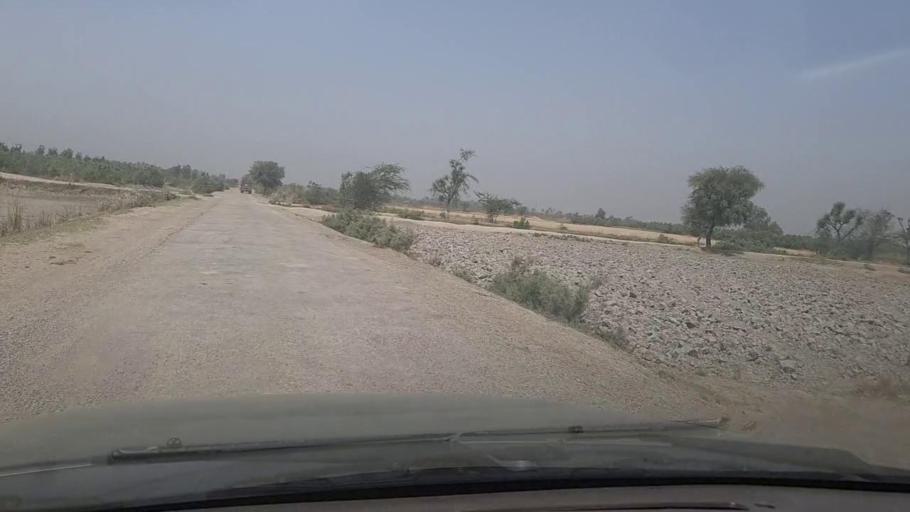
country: PK
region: Sindh
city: Madeji
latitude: 27.7974
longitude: 68.4354
